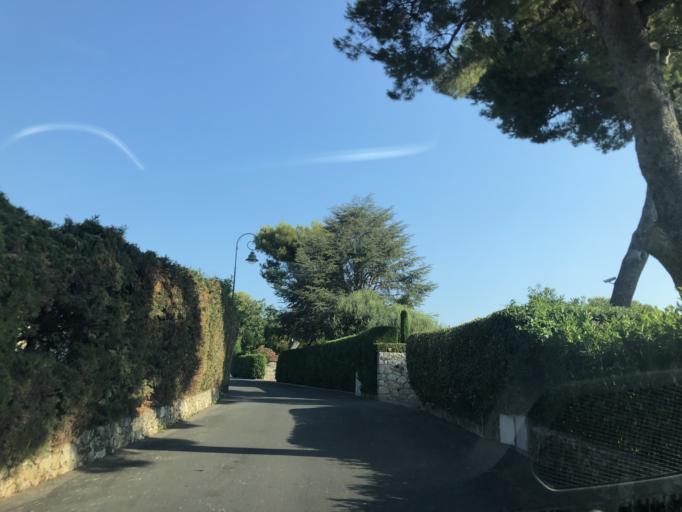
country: FR
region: Provence-Alpes-Cote d'Azur
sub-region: Departement des Alpes-Maritimes
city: Biot
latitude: 43.6230
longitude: 7.0852
